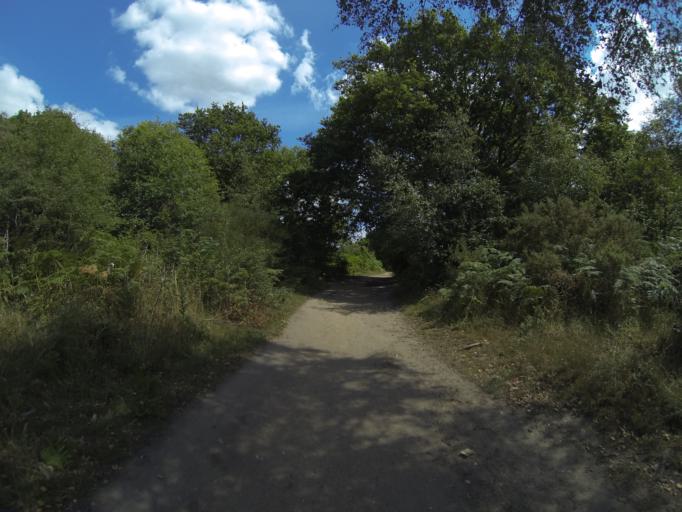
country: GB
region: England
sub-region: Kent
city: Dartford
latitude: 51.4381
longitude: 0.1888
